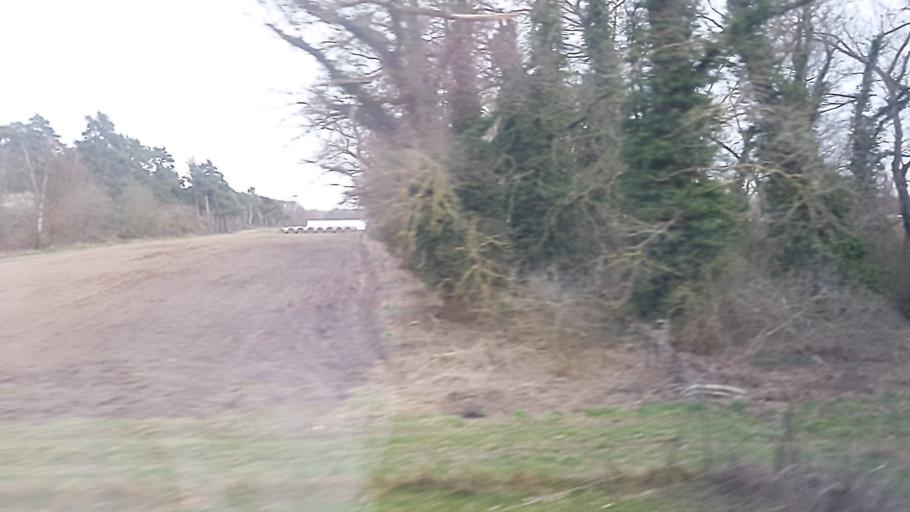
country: DE
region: Hesse
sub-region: Regierungsbezirk Darmstadt
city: Riedstadt
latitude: 49.8709
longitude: 8.4935
